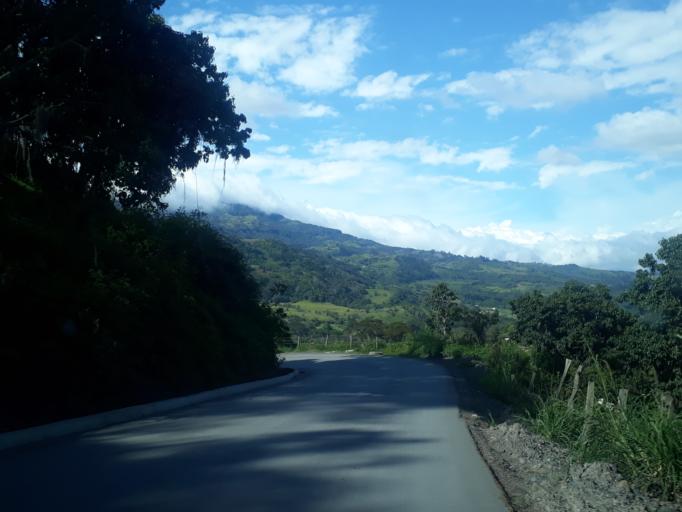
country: CO
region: Santander
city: Velez
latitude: 6.0395
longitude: -73.6523
